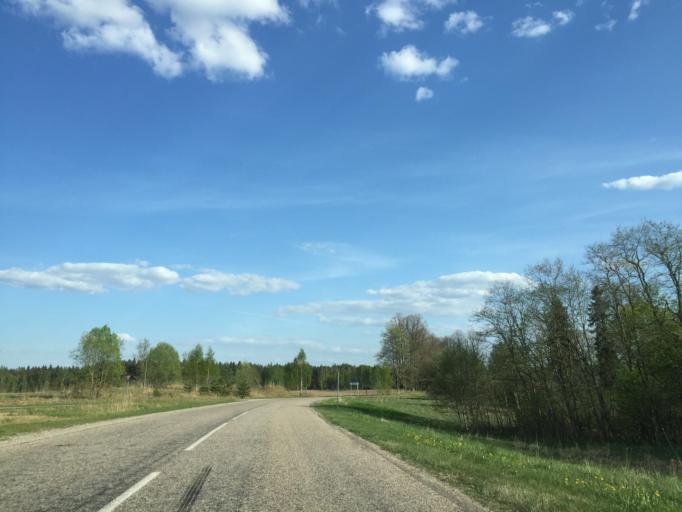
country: LV
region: Pargaujas
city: Stalbe
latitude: 57.4001
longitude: 24.9803
